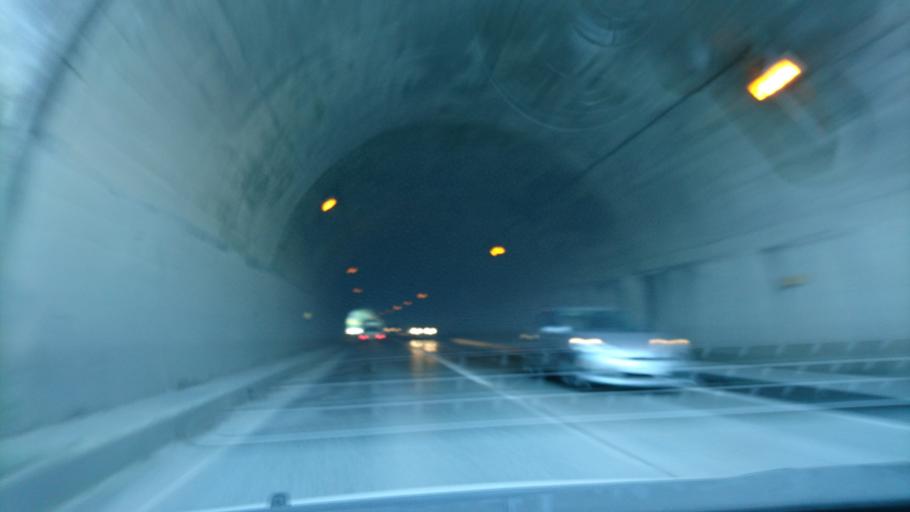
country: JP
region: Iwate
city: Ofunato
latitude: 38.9202
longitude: 141.5762
